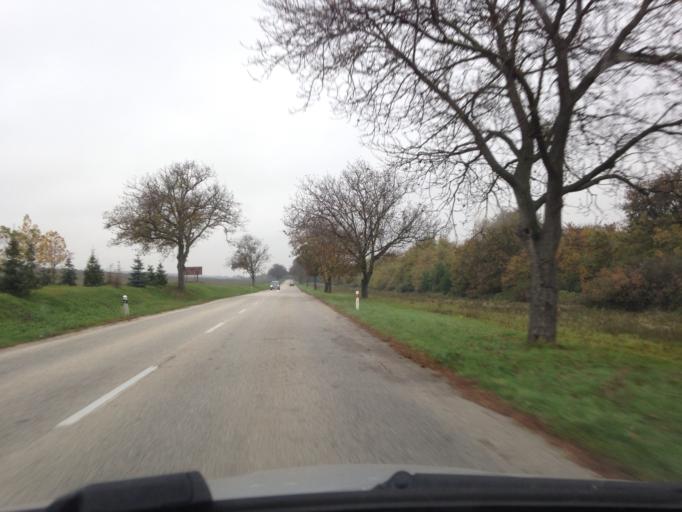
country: SK
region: Nitriansky
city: Svodin
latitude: 47.8584
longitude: 18.4876
